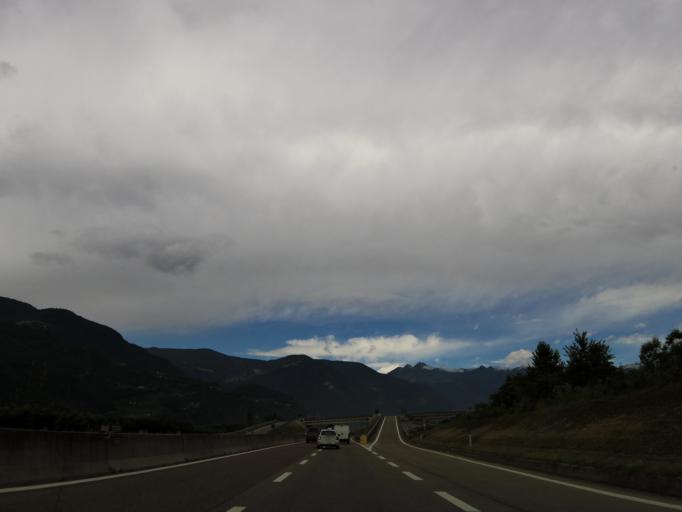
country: IT
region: Trentino-Alto Adige
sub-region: Bolzano
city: Gargazzone
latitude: 46.5744
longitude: 11.1976
